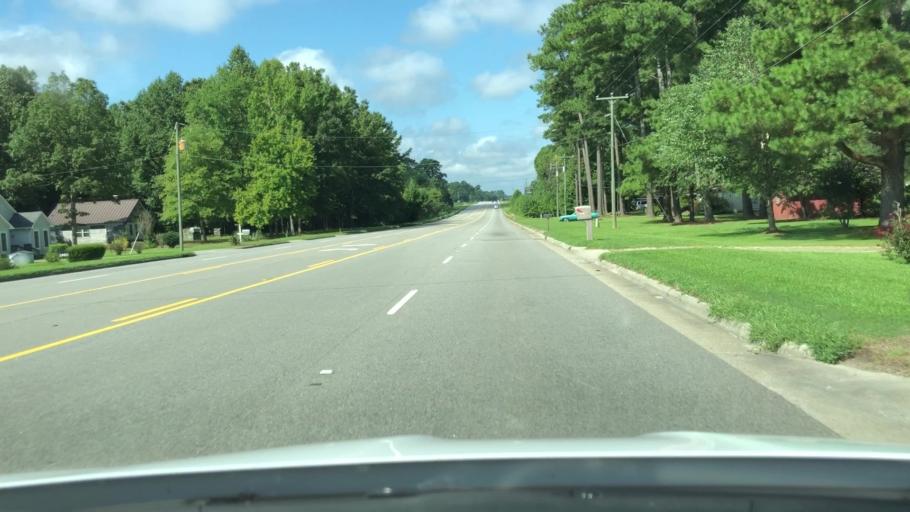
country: US
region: North Carolina
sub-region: Bertie County
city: Windsor
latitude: 36.0305
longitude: -76.7983
